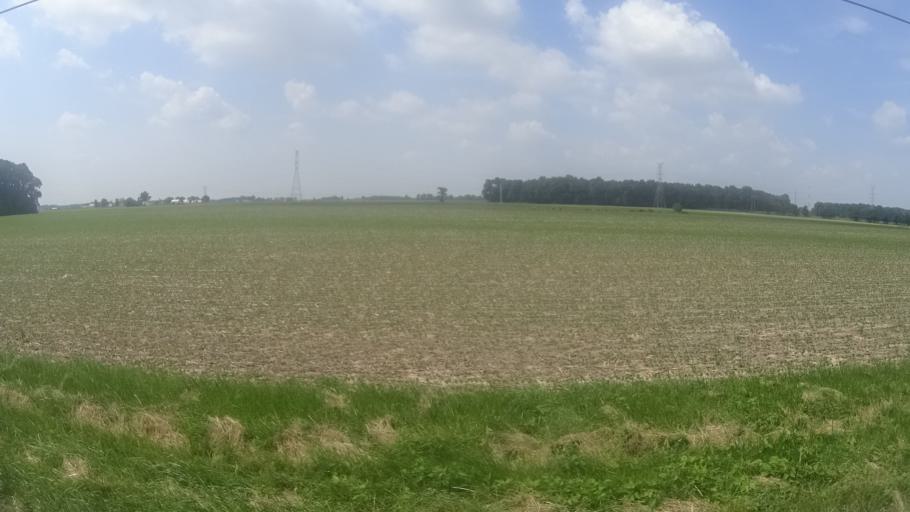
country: US
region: Ohio
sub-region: Erie County
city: Milan
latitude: 41.3442
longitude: -82.6743
